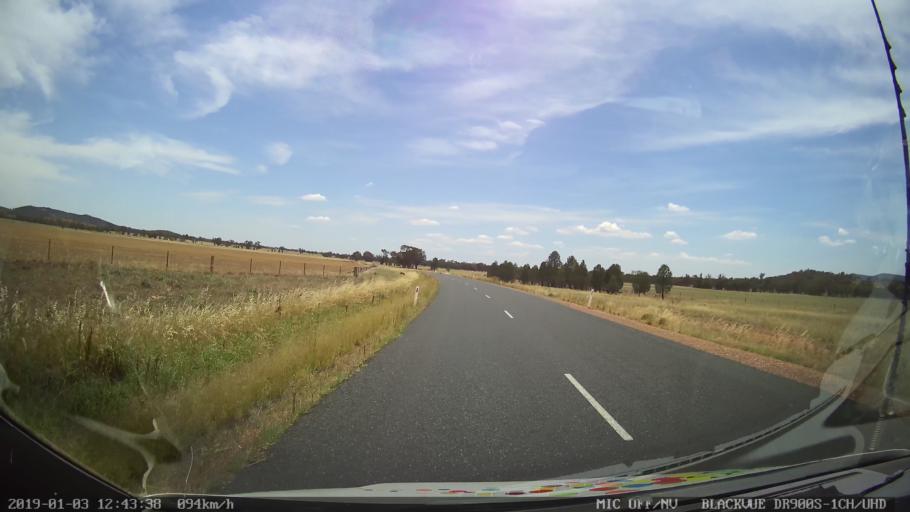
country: AU
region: New South Wales
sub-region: Weddin
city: Grenfell
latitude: -33.7726
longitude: 148.2137
